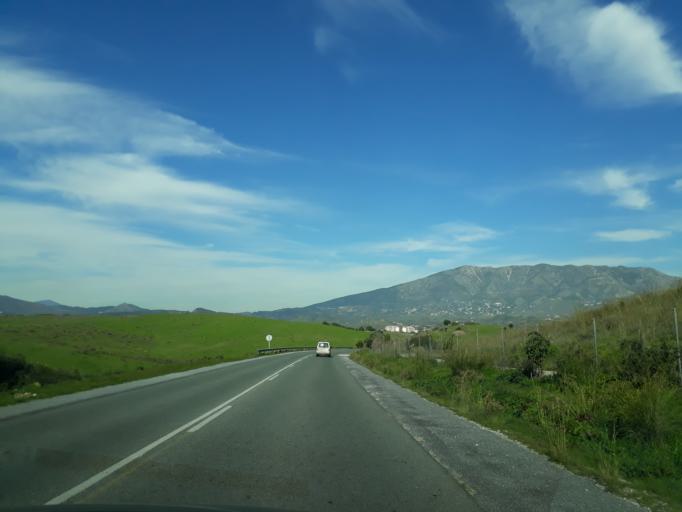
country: ES
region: Andalusia
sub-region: Provincia de Malaga
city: Fuengirola
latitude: 36.5328
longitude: -4.6860
